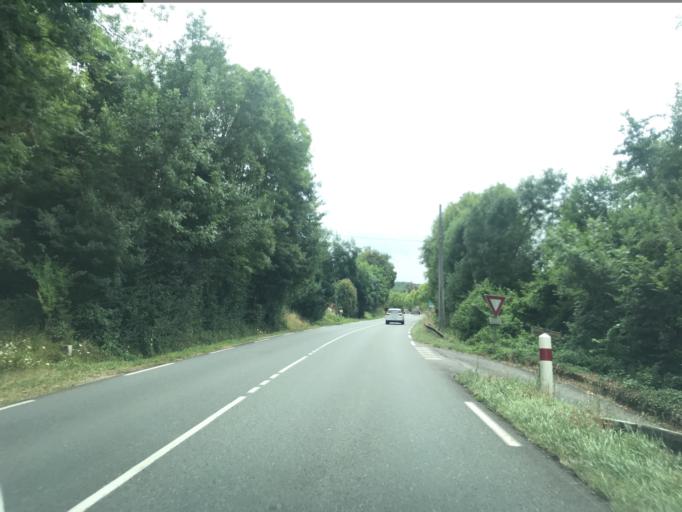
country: FR
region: Aquitaine
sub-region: Departement de la Dordogne
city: Chancelade
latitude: 45.2516
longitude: 0.6826
